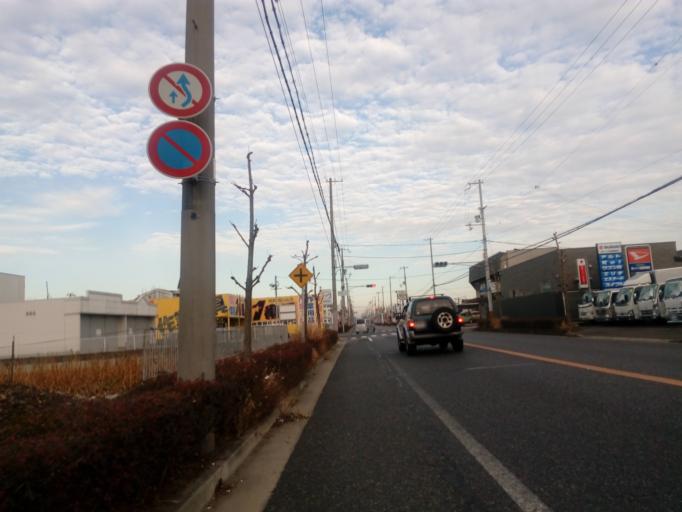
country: JP
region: Hyogo
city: Himeji
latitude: 34.7922
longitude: 134.6118
